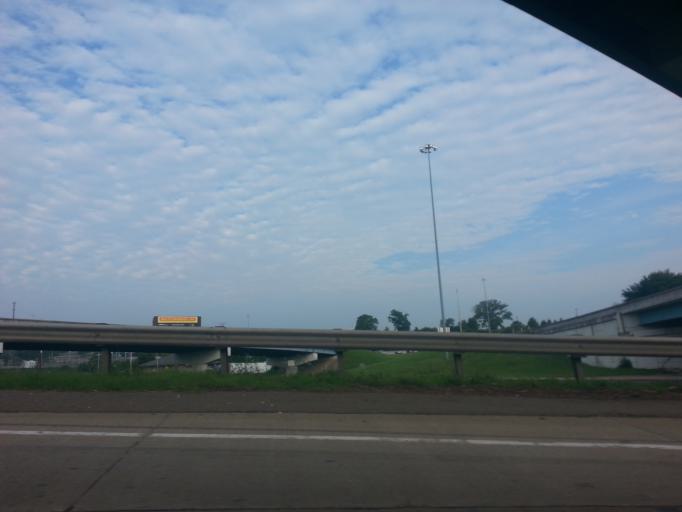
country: US
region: Tennessee
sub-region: Knox County
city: Knoxville
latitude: 35.9633
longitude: -83.9469
